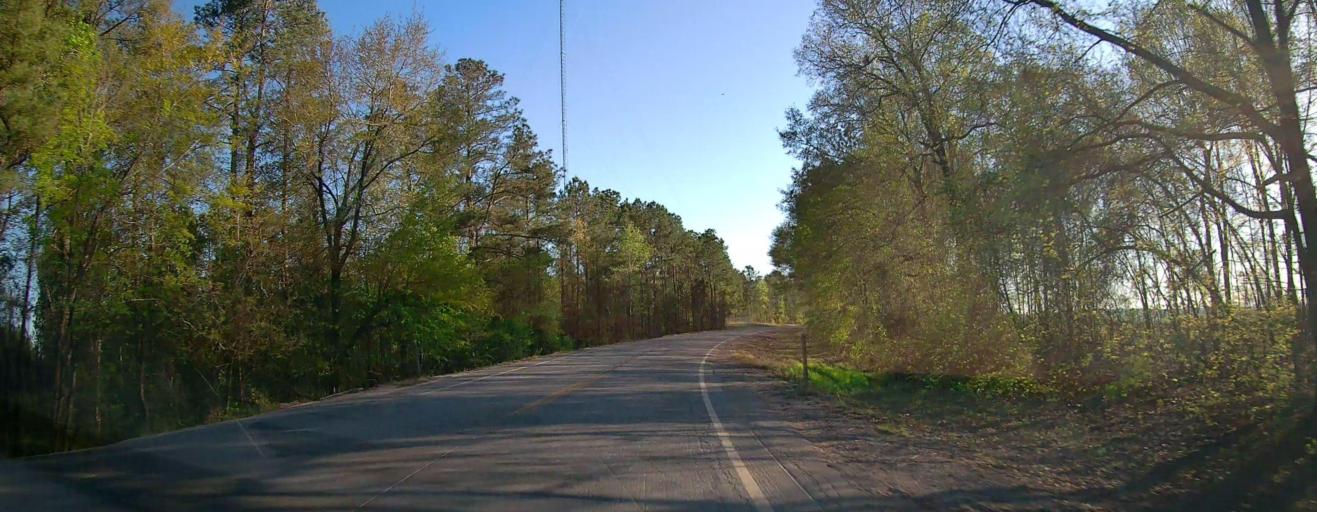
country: US
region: Georgia
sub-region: Wilkinson County
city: Irwinton
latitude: 32.8464
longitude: -83.0621
